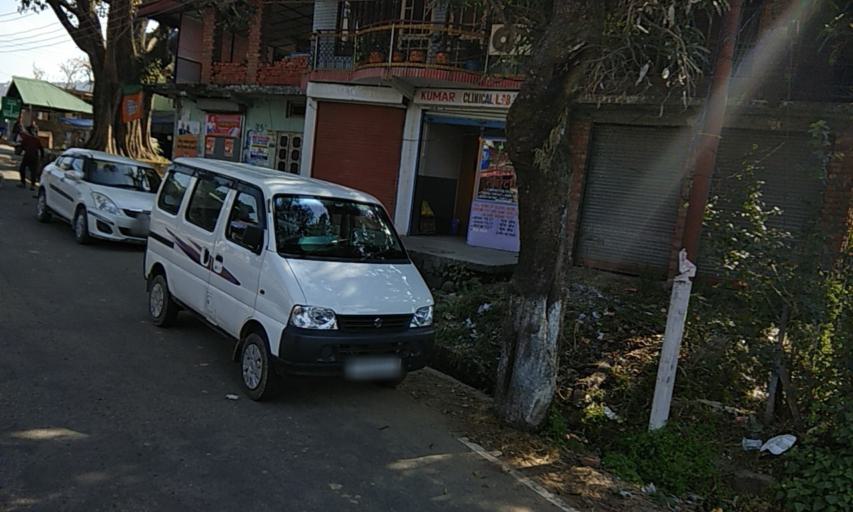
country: IN
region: Himachal Pradesh
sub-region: Kangra
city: Dharmsala
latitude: 32.1512
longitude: 76.4171
